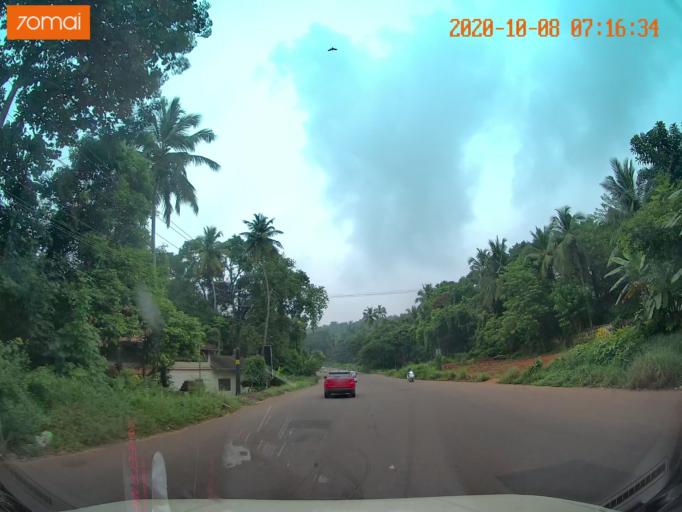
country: IN
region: Kerala
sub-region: Malappuram
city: Ponnani
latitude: 10.8318
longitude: 76.0195
